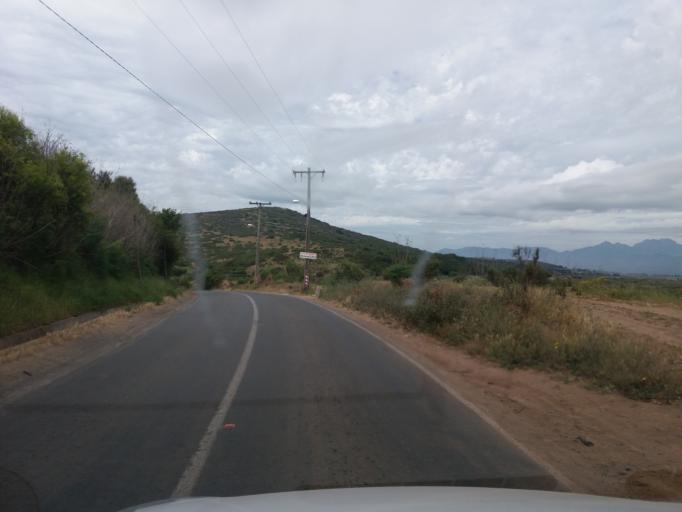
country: CL
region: Valparaiso
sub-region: Provincia de Marga Marga
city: Quilpue
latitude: -32.9166
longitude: -71.4315
